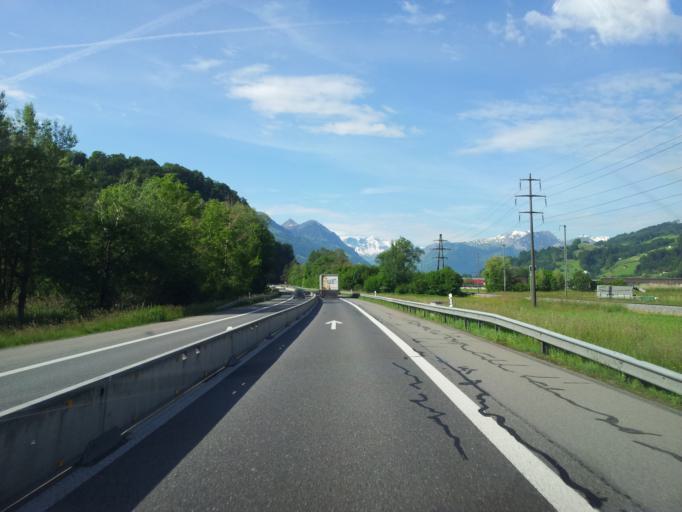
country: CH
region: Obwalden
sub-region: Obwalden
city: Kerns
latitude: 46.9178
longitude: 8.2685
